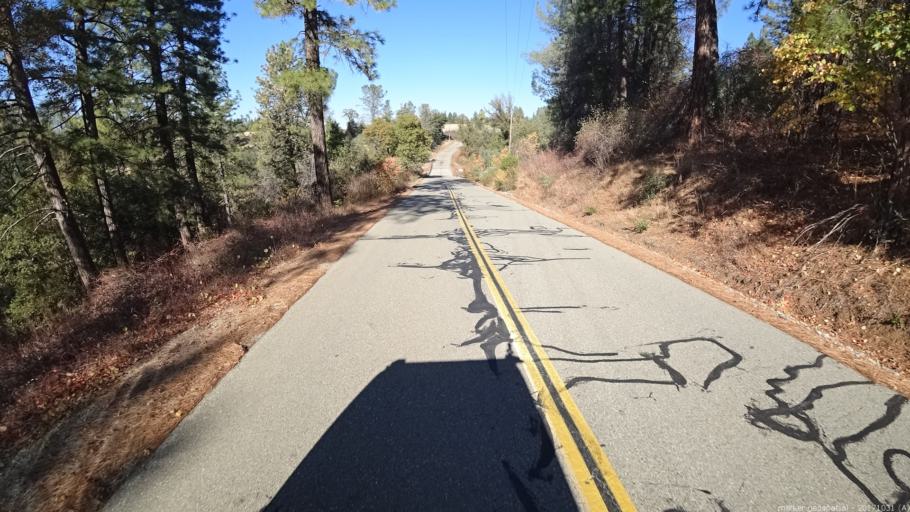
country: US
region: California
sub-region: Shasta County
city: Shingletown
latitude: 40.4669
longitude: -122.0037
